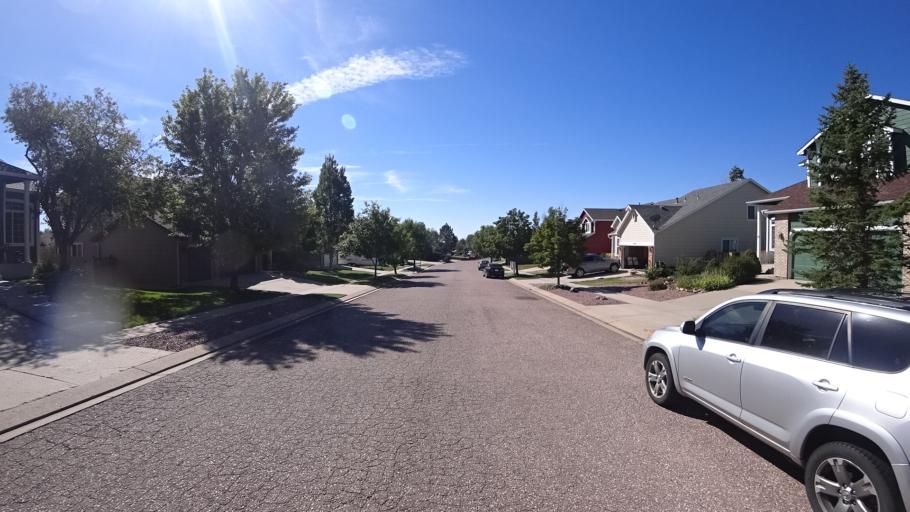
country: US
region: Colorado
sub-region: El Paso County
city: Black Forest
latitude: 38.9520
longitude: -104.7291
